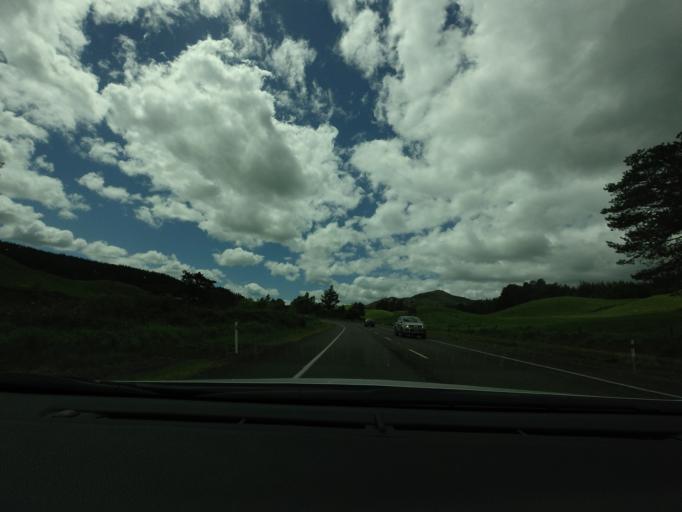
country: NZ
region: Bay of Plenty
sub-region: Rotorua District
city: Rotorua
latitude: -38.3342
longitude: 176.3669
